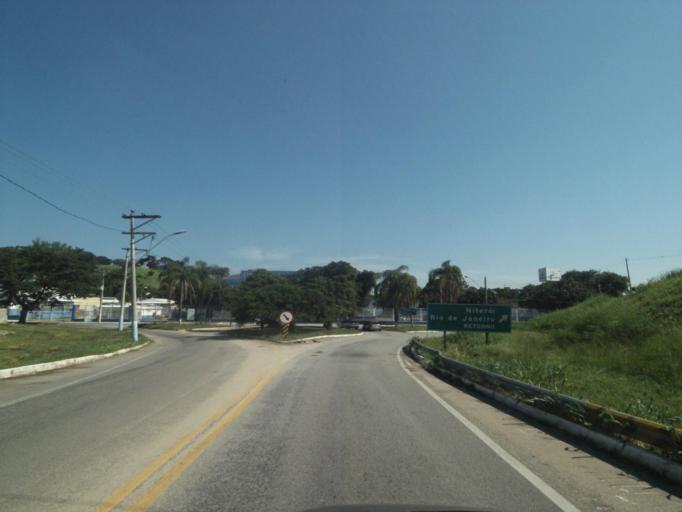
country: BR
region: Rio de Janeiro
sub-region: Niteroi
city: Niteroi
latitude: -22.8439
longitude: -43.0968
